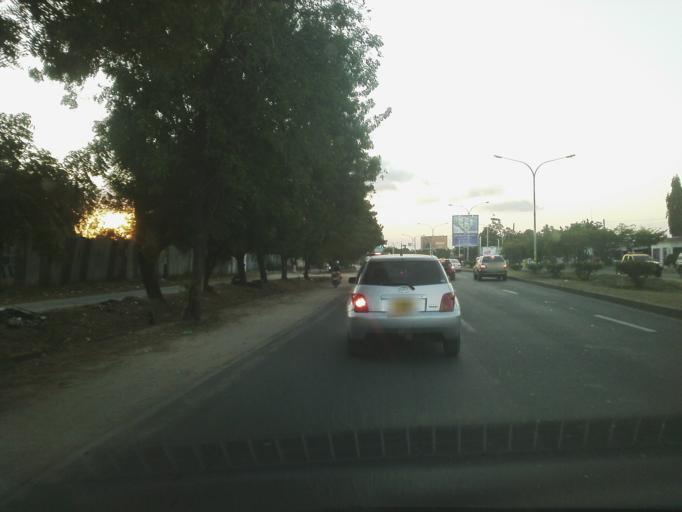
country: TZ
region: Dar es Salaam
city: Magomeni
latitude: -6.7797
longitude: 39.2721
